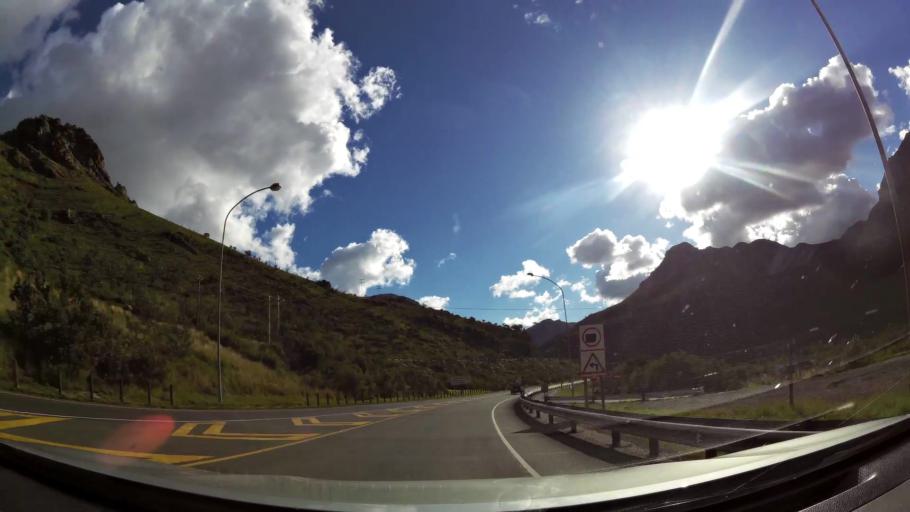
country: ZA
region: Western Cape
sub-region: Cape Winelands District Municipality
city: Paarl
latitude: -33.7332
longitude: 19.1210
